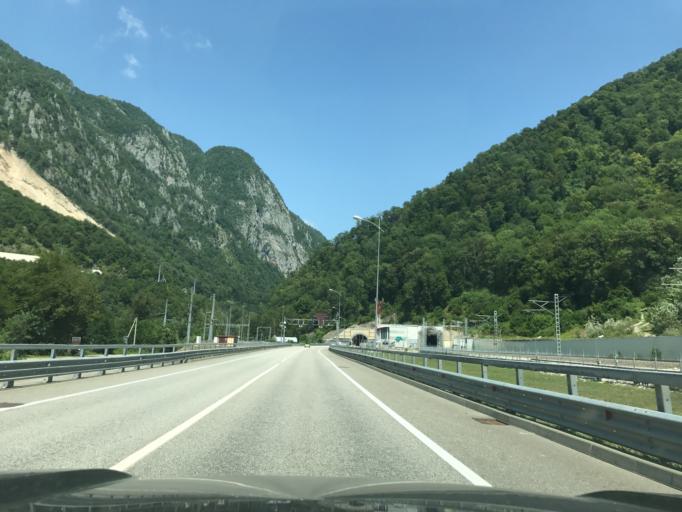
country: RU
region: Krasnodarskiy
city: Vysokoye
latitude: 43.5875
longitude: 40.0141
